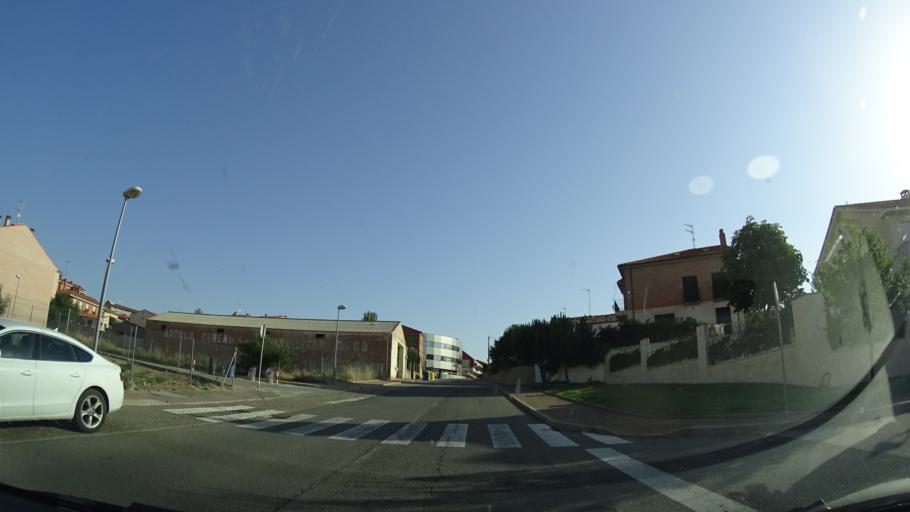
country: ES
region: Castille and Leon
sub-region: Provincia de Burgos
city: Lerma
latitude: 42.0229
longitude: -3.7545
